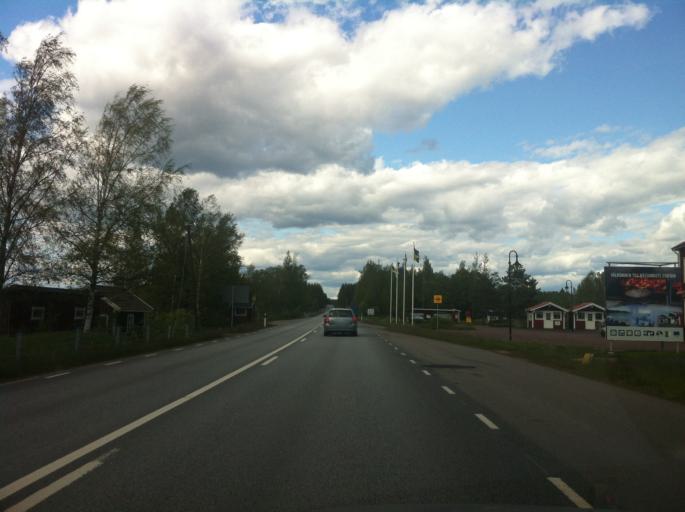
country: SE
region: Vaermland
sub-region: Storfors Kommun
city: Storfors
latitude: 59.4342
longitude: 14.2303
